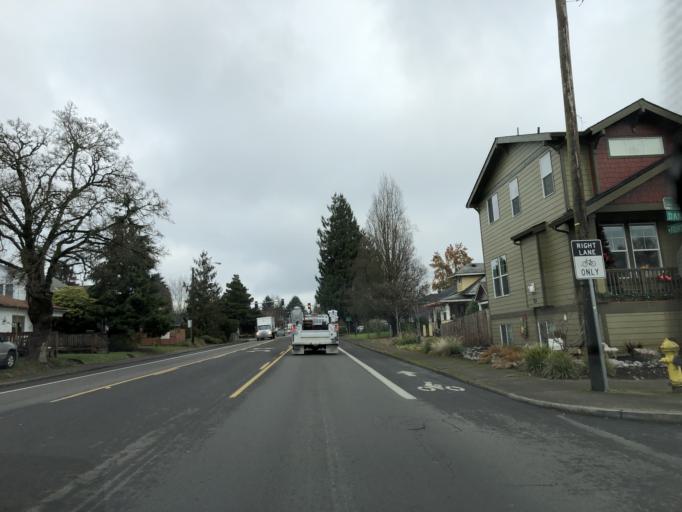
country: US
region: Washington
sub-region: Clark County
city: Vancouver
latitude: 45.6402
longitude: -122.6752
